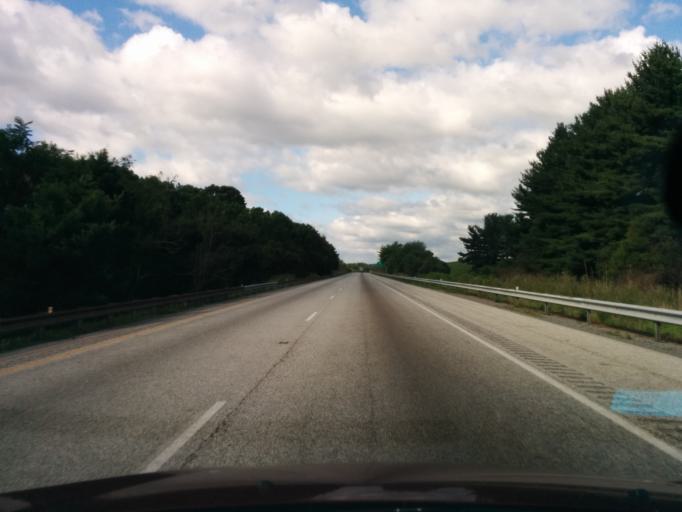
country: US
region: Virginia
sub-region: Rockbridge County
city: Glasgow
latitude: 37.6858
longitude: -79.4886
